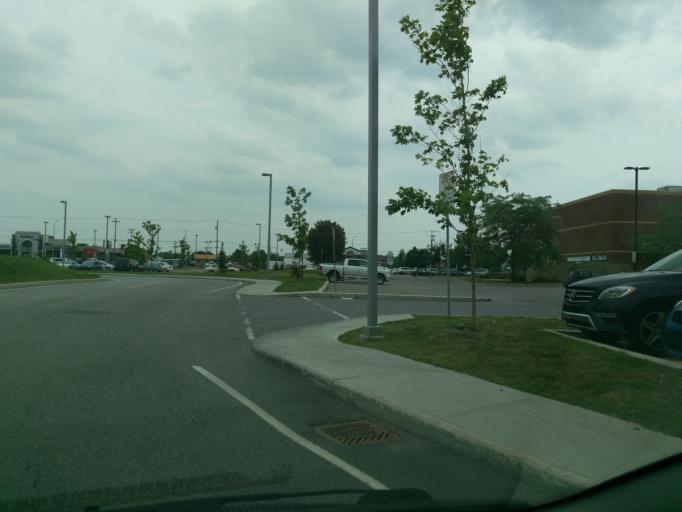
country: CA
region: Quebec
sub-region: Outaouais
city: Gatineau
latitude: 45.4820
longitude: -75.6860
